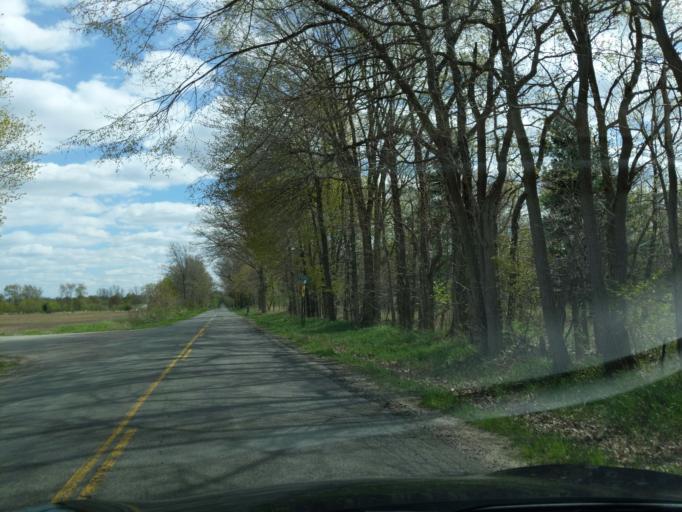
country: US
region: Michigan
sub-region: Eaton County
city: Eaton Rapids
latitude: 42.5022
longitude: -84.5464
